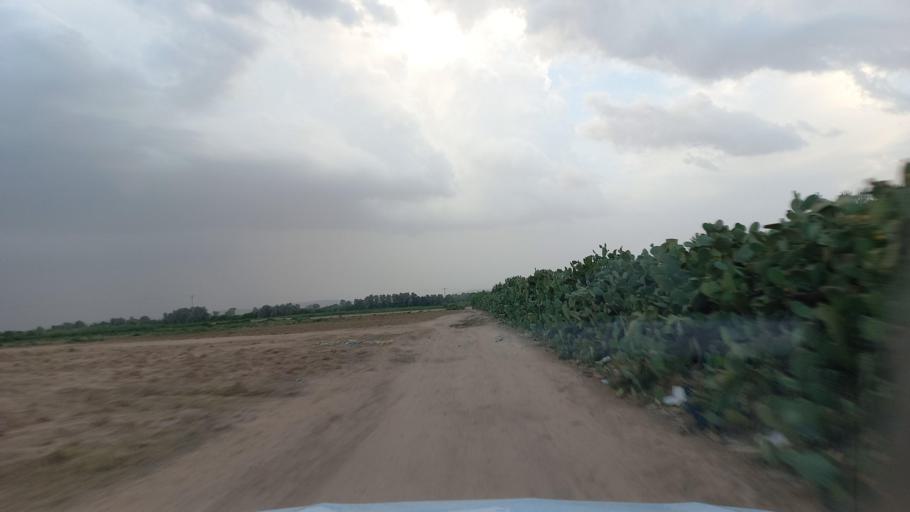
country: TN
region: Al Qasrayn
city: Kasserine
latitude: 35.2767
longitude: 9.0589
